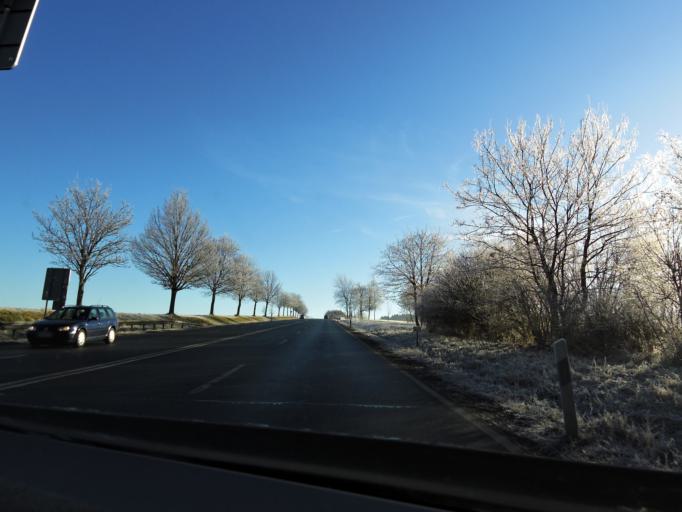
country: DE
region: Bavaria
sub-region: Upper Franconia
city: Bad Alexandersbad
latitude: 50.0201
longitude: 12.0303
